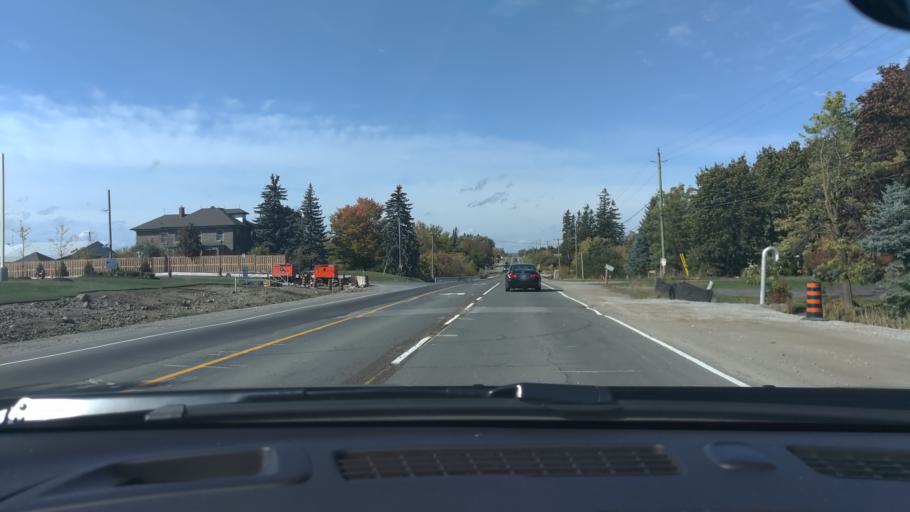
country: CA
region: Ontario
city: Brampton
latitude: 43.7705
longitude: -79.8033
